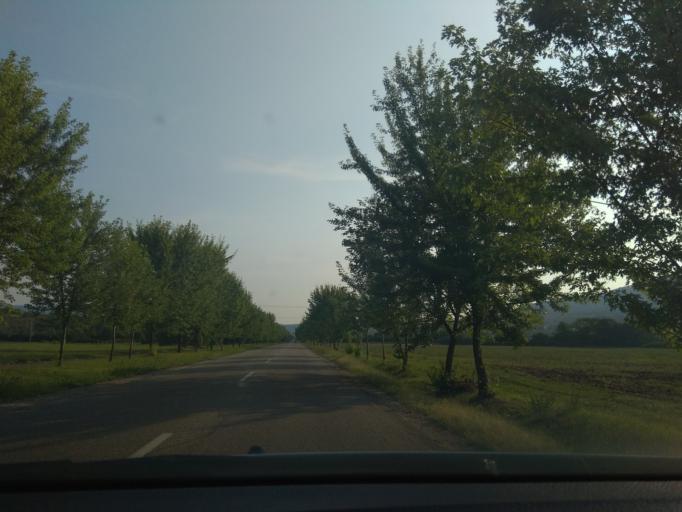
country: HU
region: Heves
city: Felsotarkany
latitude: 47.9572
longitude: 20.3950
